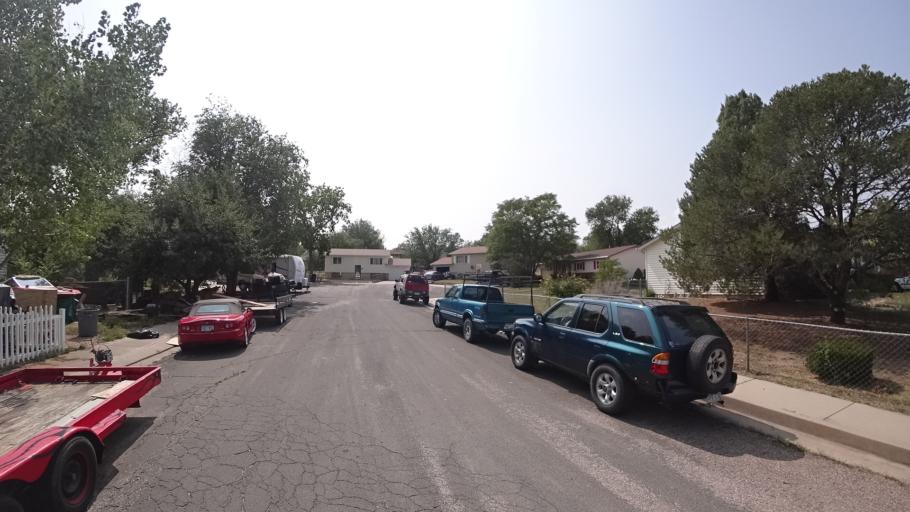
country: US
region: Colorado
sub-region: El Paso County
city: Stratmoor
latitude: 38.8050
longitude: -104.7641
